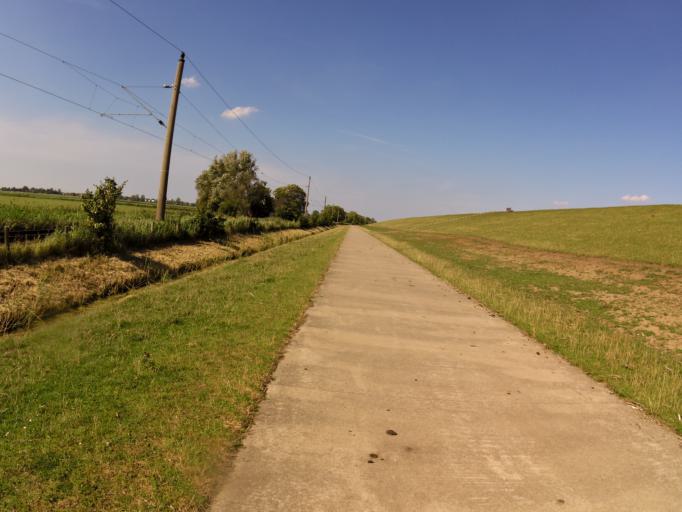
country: DE
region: Lower Saxony
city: Nordenham
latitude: 53.4526
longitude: 8.4751
